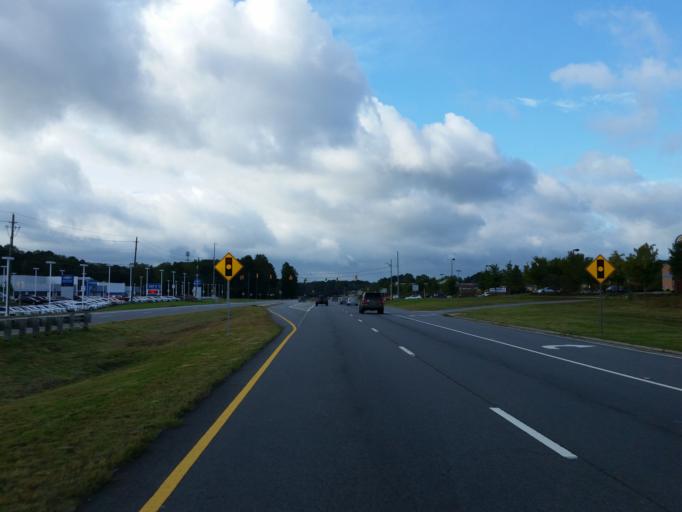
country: US
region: Georgia
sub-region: Cobb County
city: Acworth
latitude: 34.0434
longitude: -84.6958
